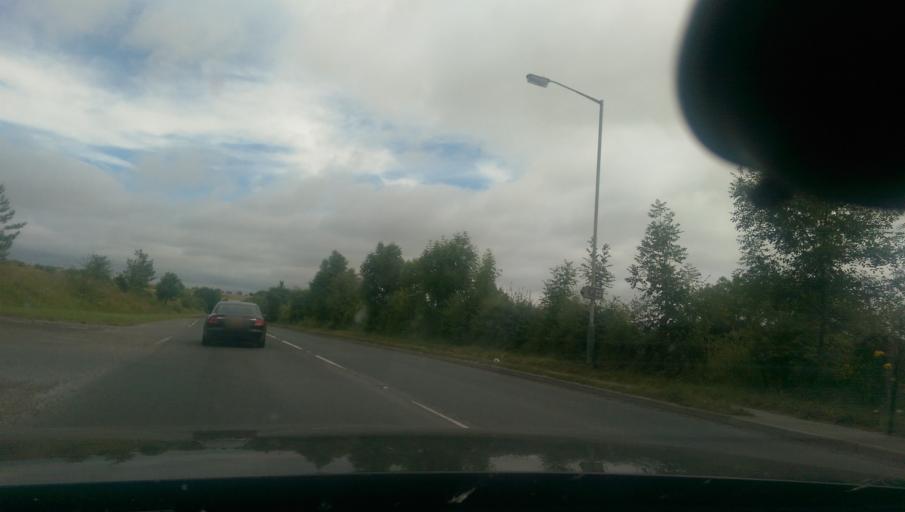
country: GB
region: England
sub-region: Wiltshire
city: Amesbury
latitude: 51.1882
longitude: -1.7835
